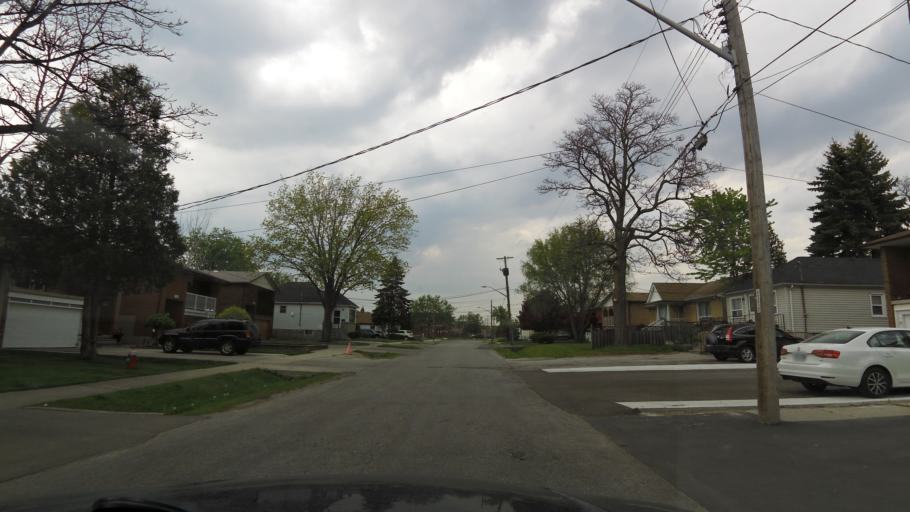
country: CA
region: Ontario
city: Etobicoke
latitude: 43.5732
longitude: -79.5647
